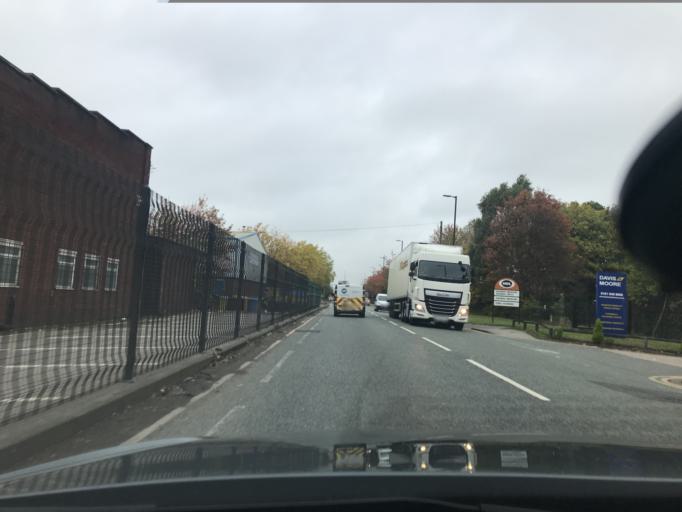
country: GB
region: England
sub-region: Trafford
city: Trafford Park
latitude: 53.4733
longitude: -2.3177
